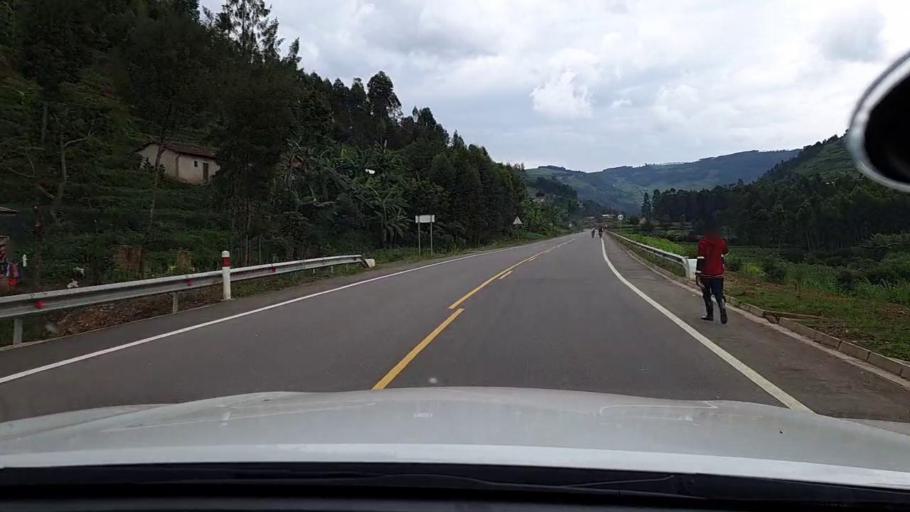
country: RW
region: Northern Province
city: Byumba
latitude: -1.6333
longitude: 29.9277
